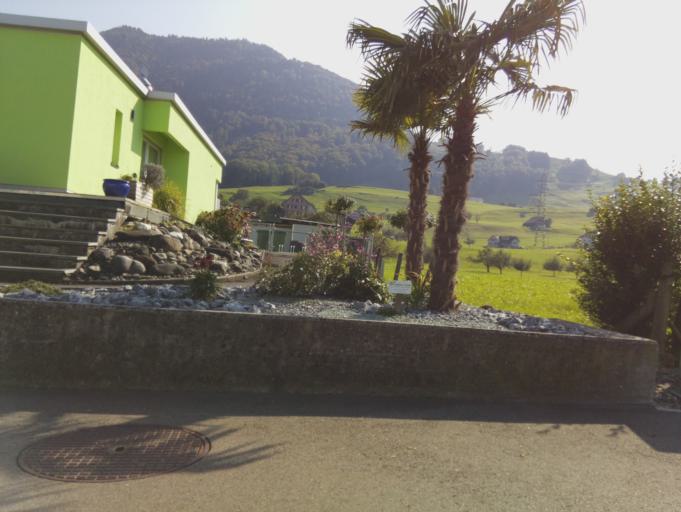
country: CH
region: Schwyz
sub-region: Bezirk March
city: Schubelbach
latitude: 47.1733
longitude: 8.9046
